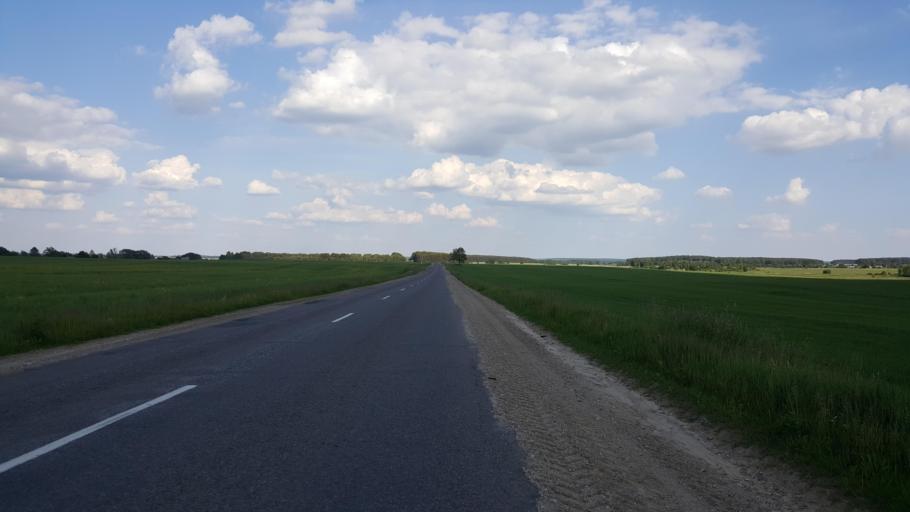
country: BY
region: Brest
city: Kamyanyets
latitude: 52.4129
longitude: 23.7153
